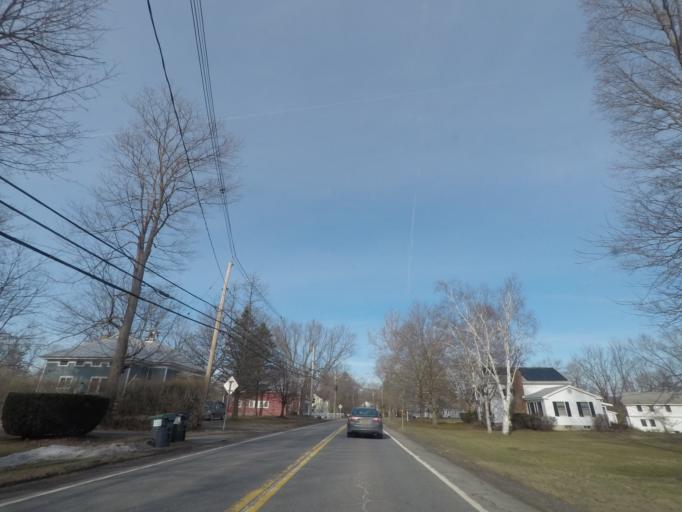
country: US
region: New York
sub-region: Columbia County
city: Niverville
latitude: 42.4676
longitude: -73.6322
